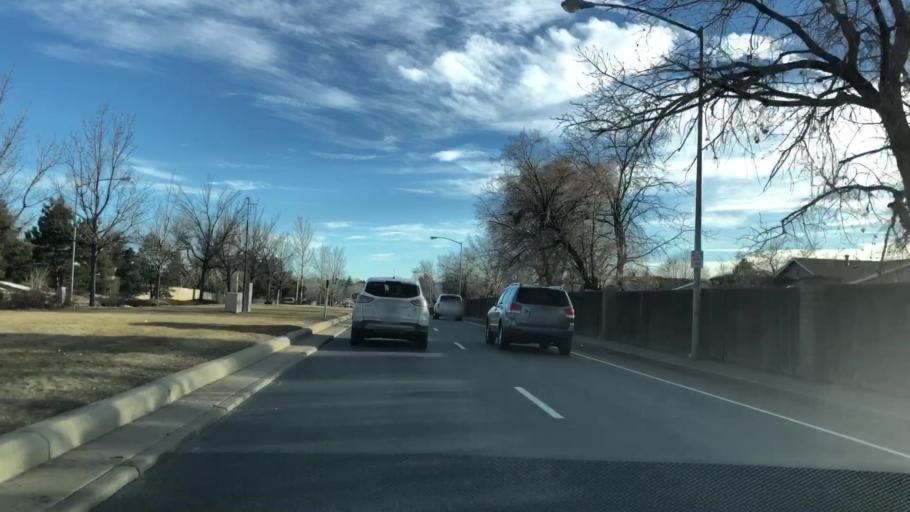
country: US
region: Colorado
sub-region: Arapahoe County
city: Dove Valley
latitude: 39.6427
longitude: -104.7918
